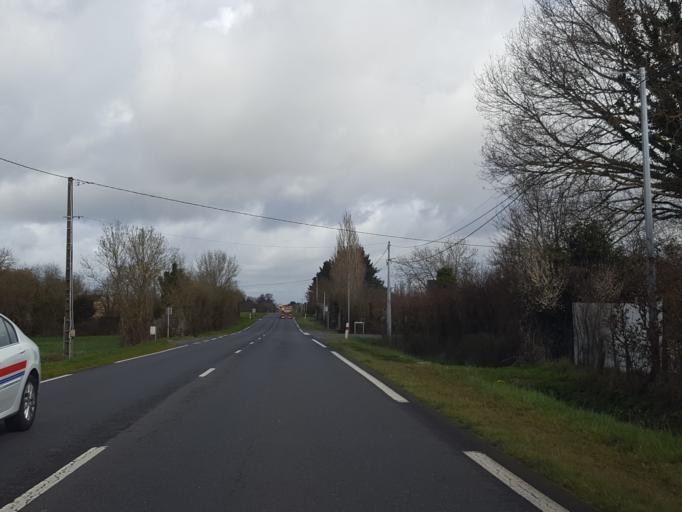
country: FR
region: Pays de la Loire
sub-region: Departement de la Loire-Atlantique
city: Le Bignon
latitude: 47.0962
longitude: -1.5321
